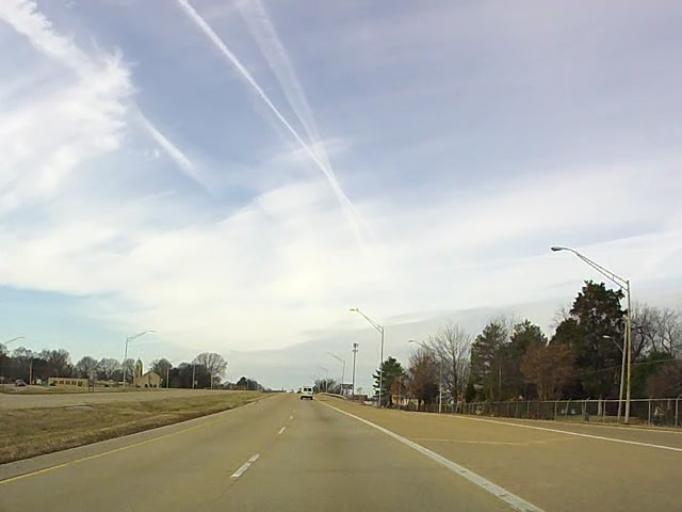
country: US
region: Tennessee
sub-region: Shelby County
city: Bartlett
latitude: 35.1482
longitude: -89.9429
